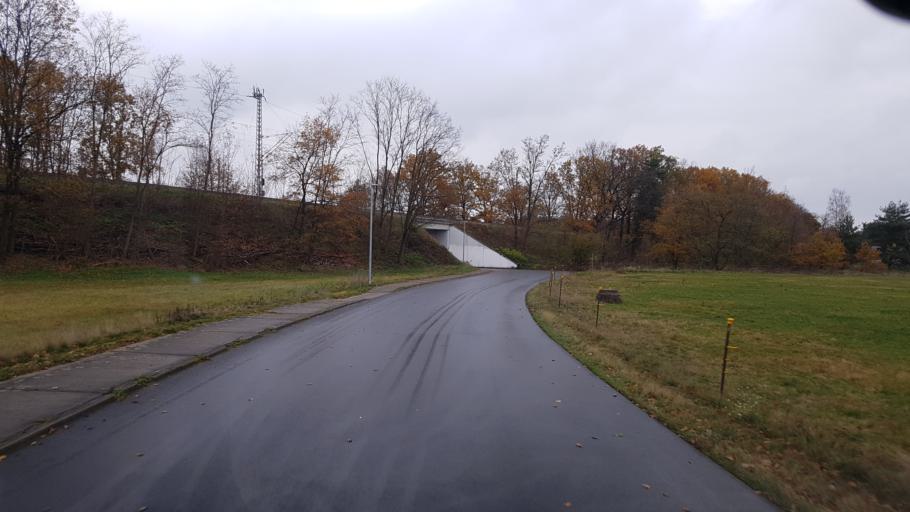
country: DE
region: Brandenburg
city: Ortrand
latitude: 51.3775
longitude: 13.7696
